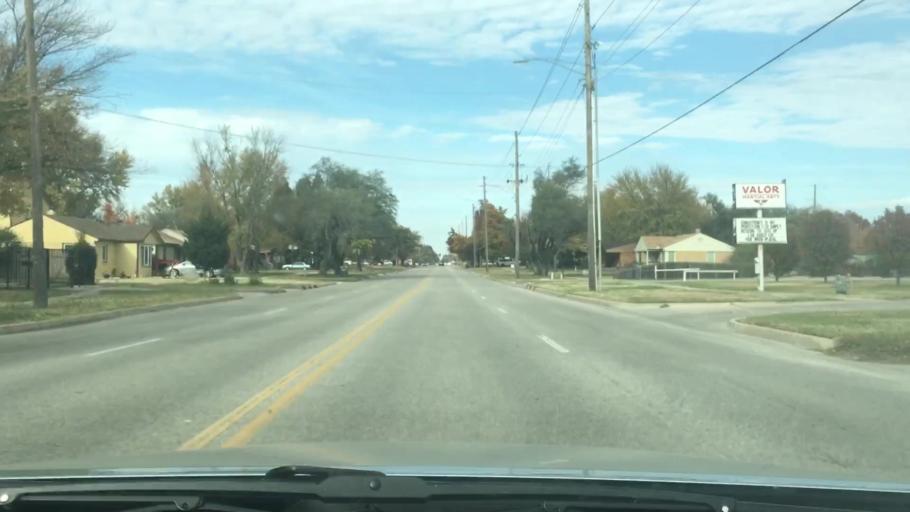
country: US
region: Kansas
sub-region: Sedgwick County
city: Wichita
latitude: 37.6597
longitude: -97.2621
